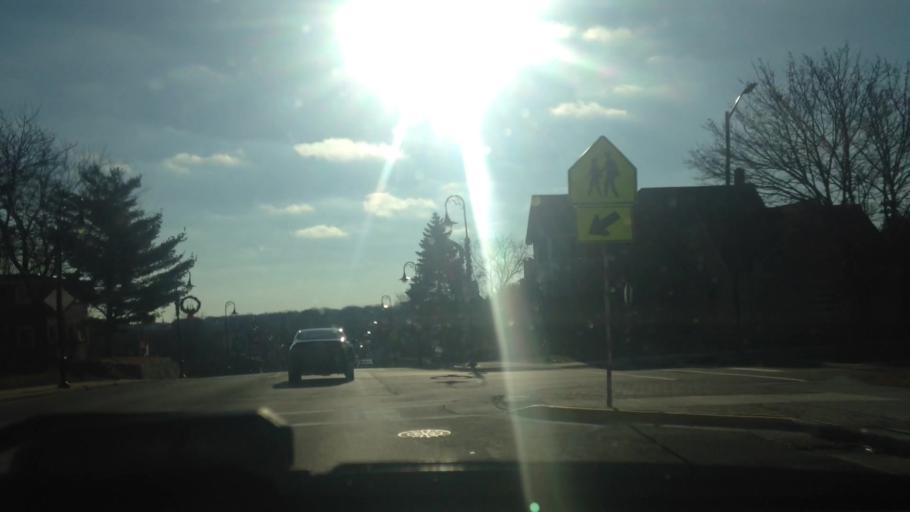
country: US
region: Wisconsin
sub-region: Waukesha County
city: Menomonee Falls
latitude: 43.1778
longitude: -88.1162
